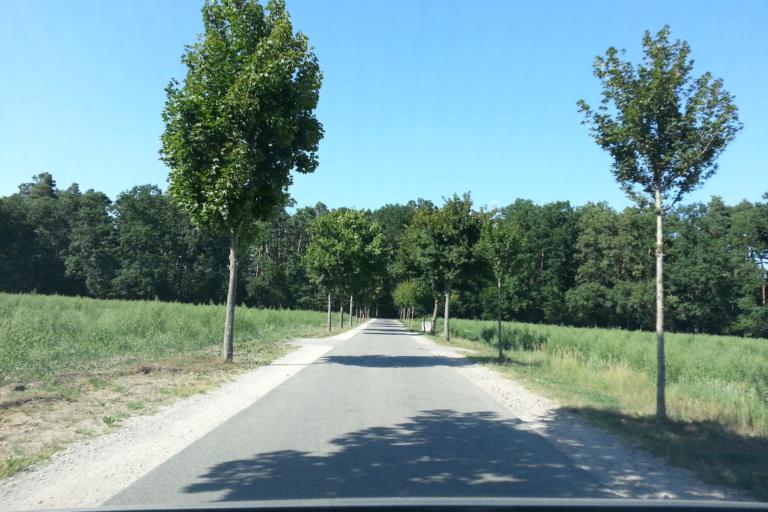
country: DE
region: Mecklenburg-Vorpommern
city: Torgelow
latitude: 53.6481
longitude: 14.0283
